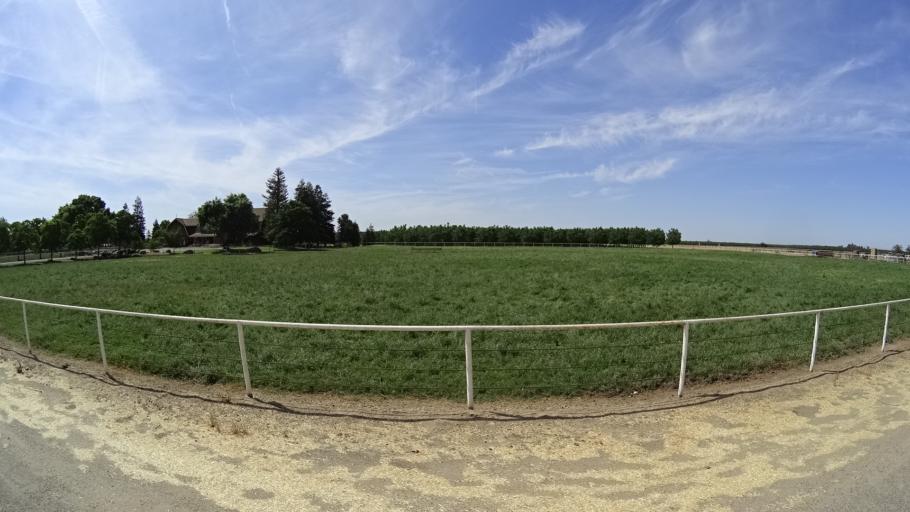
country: US
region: California
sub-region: Kings County
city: Hanford
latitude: 36.3571
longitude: -119.5978
